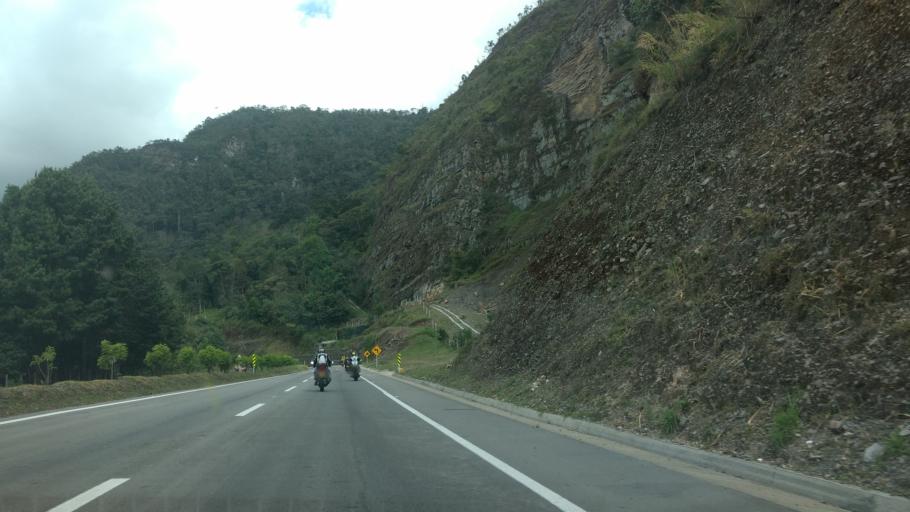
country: CO
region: Cundinamarca
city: San Francisco
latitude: 4.9461
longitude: -74.2935
